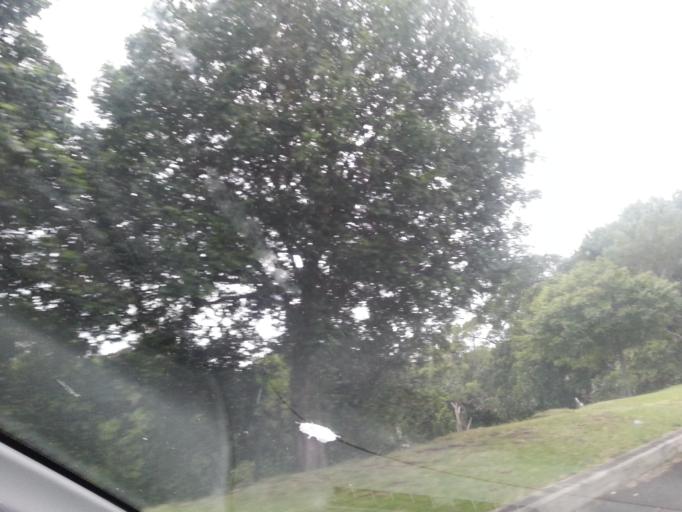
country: AU
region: New South Wales
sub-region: Wollongong
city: Keiraville
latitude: -34.4116
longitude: 150.8627
